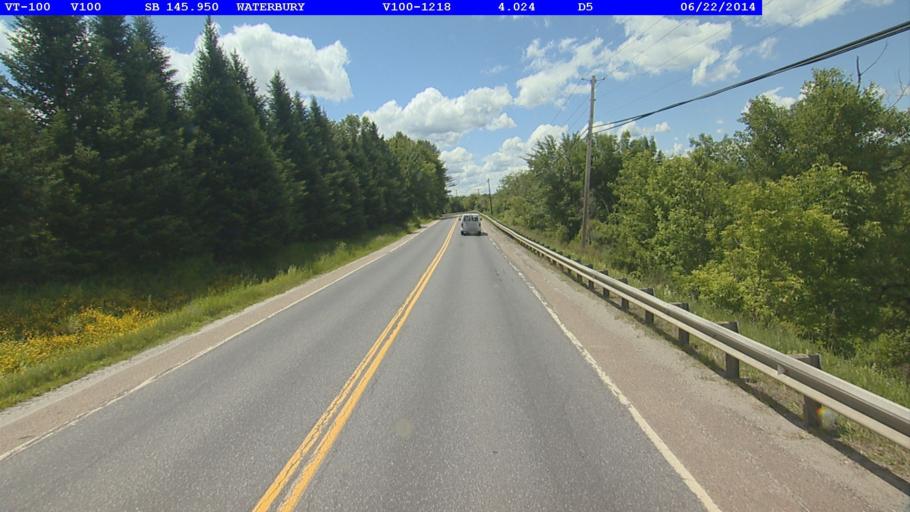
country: US
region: Vermont
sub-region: Washington County
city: Waterbury
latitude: 44.3869
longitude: -72.7198
